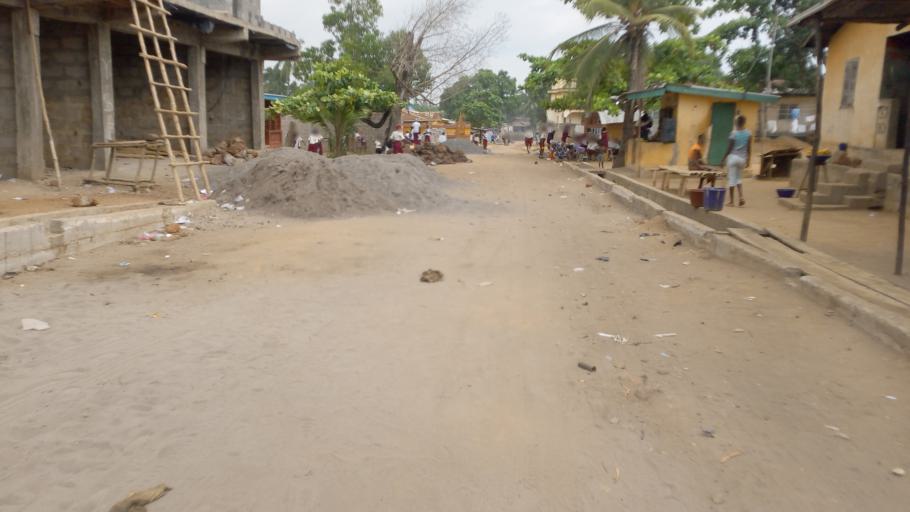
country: SL
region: Western Area
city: Waterloo
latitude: 8.3265
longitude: -13.0609
